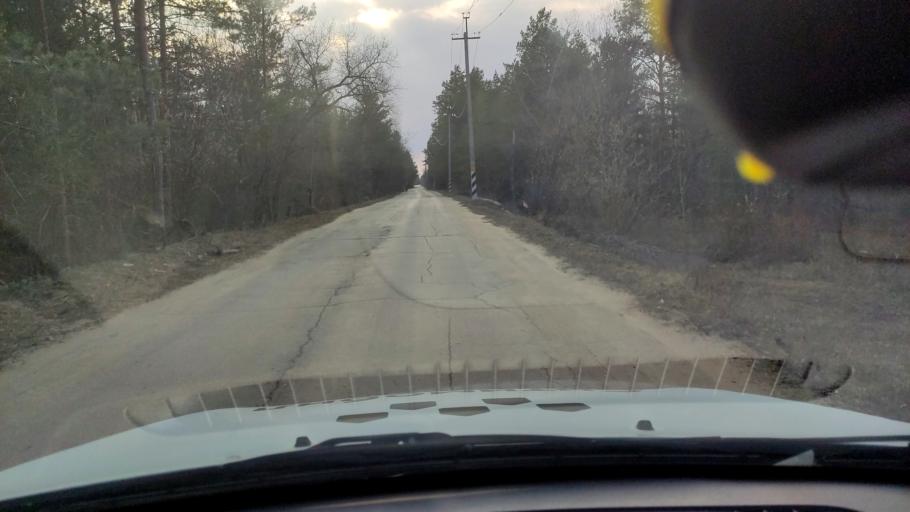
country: RU
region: Samara
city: Zhigulevsk
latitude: 53.4585
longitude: 49.6159
